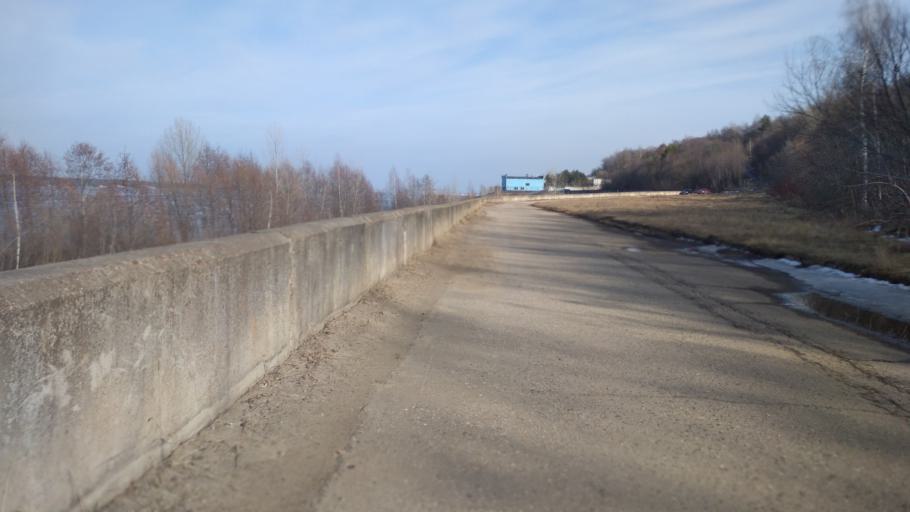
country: RU
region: Chuvashia
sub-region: Cheboksarskiy Rayon
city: Cheboksary
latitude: 56.1451
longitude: 47.3219
